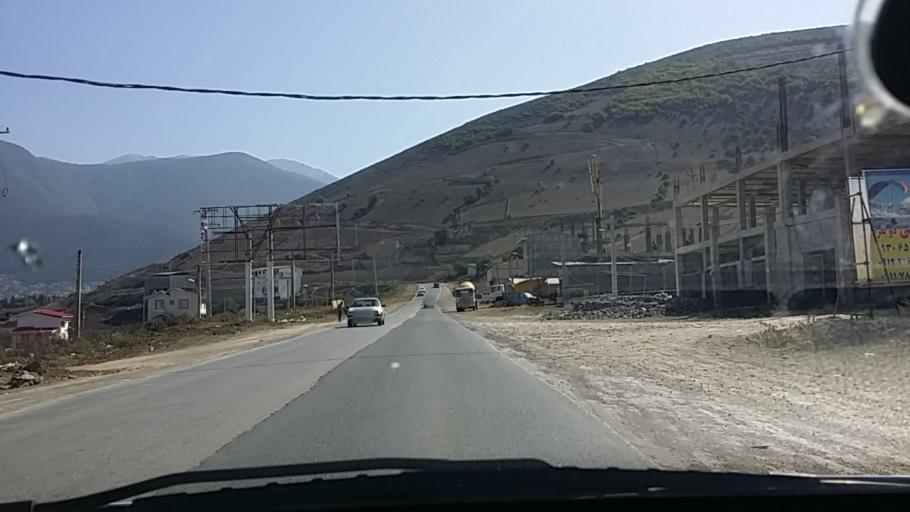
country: IR
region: Mazandaran
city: `Abbasabad
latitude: 36.5197
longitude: 51.1588
